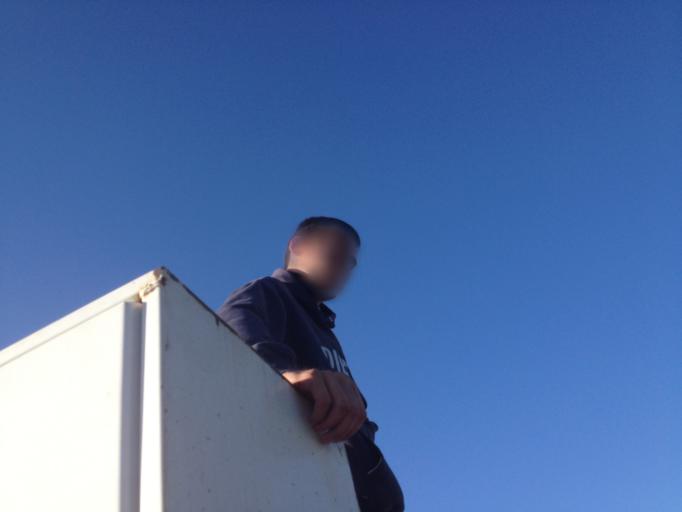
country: US
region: Kansas
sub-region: Barton County
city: Great Bend
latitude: 38.3028
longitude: -98.6797
